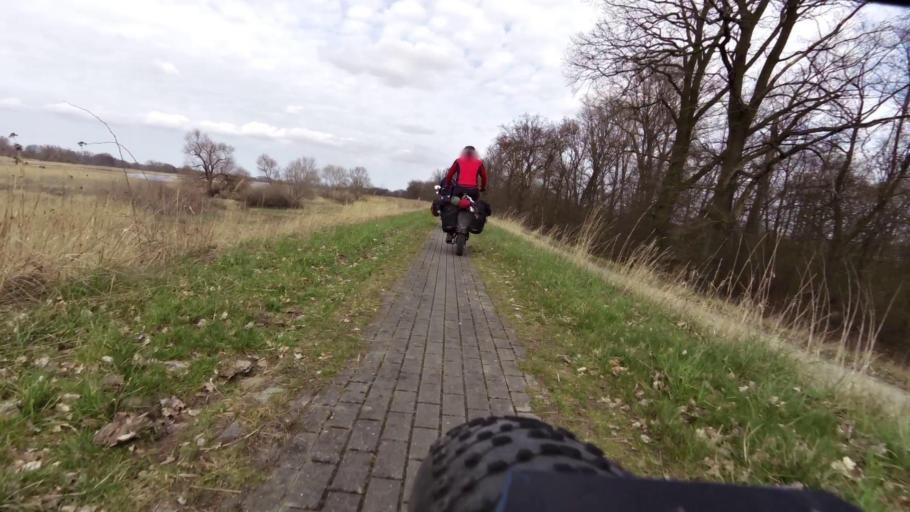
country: PL
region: Lubusz
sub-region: Powiat slubicki
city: Gorzyca
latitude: 52.4818
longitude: 14.6282
